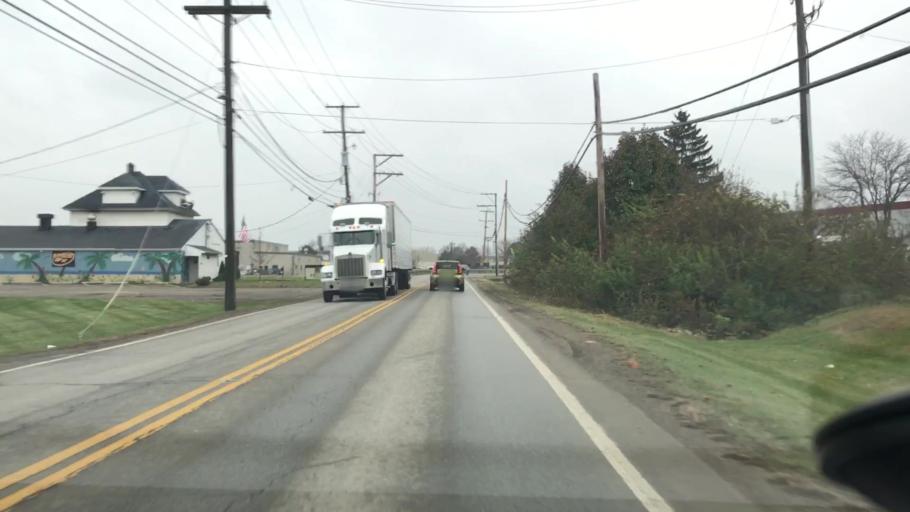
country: US
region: Ohio
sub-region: Franklin County
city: Upper Arlington
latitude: 40.0028
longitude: -83.1090
